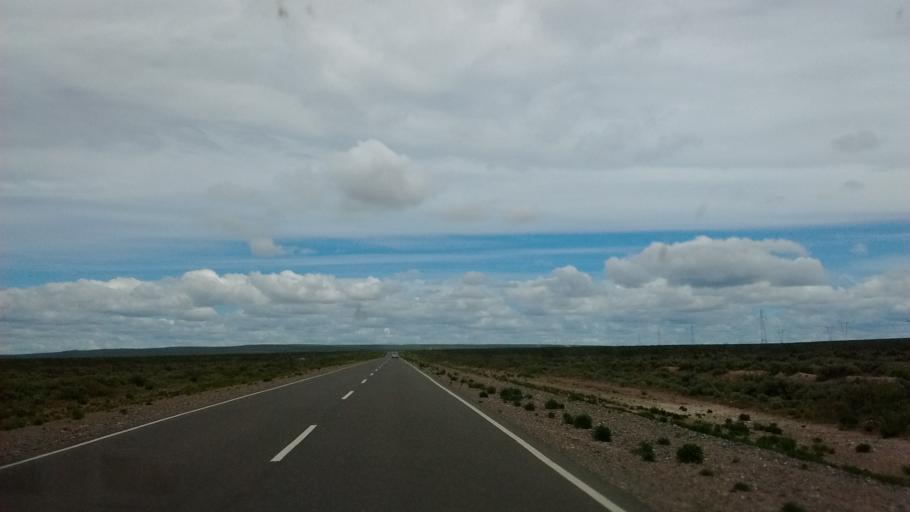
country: AR
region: Neuquen
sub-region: Departamento de Picun Leufu
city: Picun Leufu
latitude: -39.7029
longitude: -69.4987
